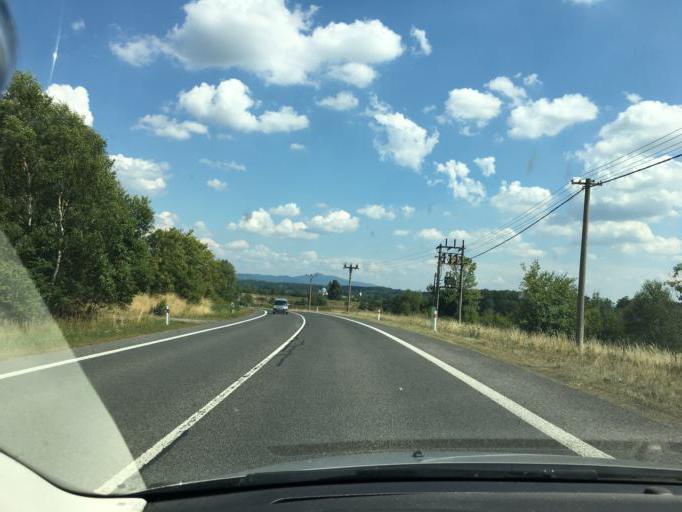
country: CZ
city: Jablonne v Podjestedi
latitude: 50.7704
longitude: 14.7300
